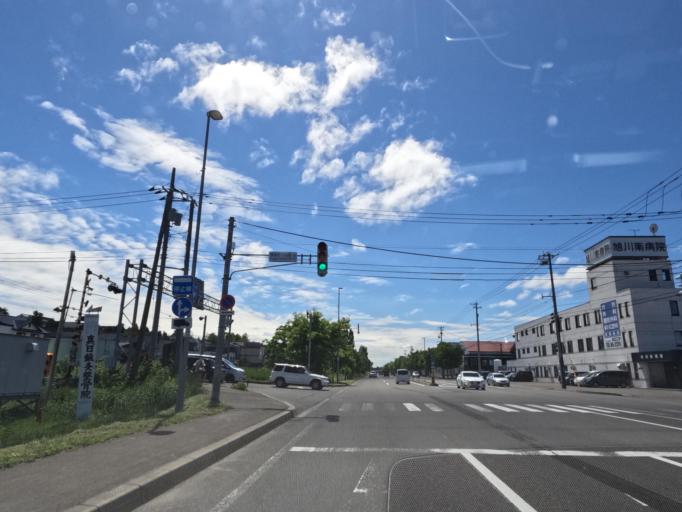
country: JP
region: Hokkaido
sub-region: Asahikawa-shi
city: Asahikawa
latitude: 43.7354
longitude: 142.3629
